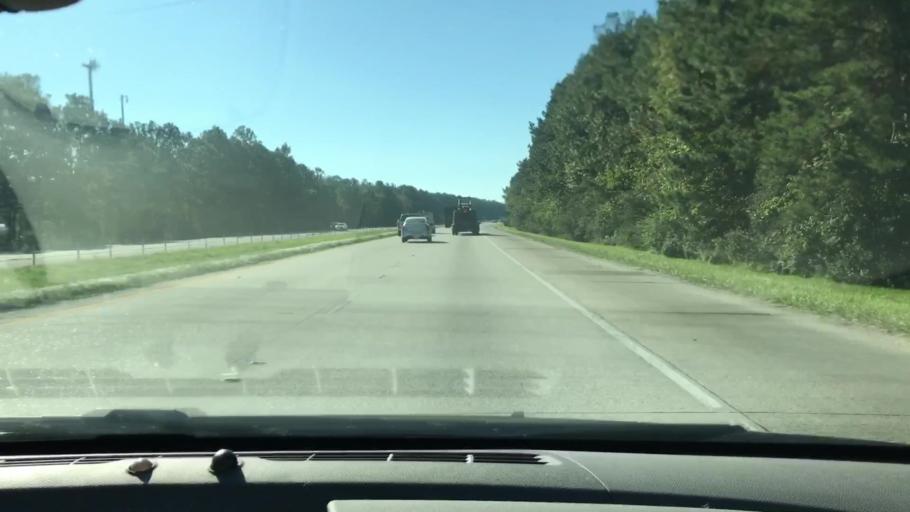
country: US
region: Louisiana
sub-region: Saint Tammany Parish
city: Pearl River
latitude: 30.3435
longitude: -89.7389
